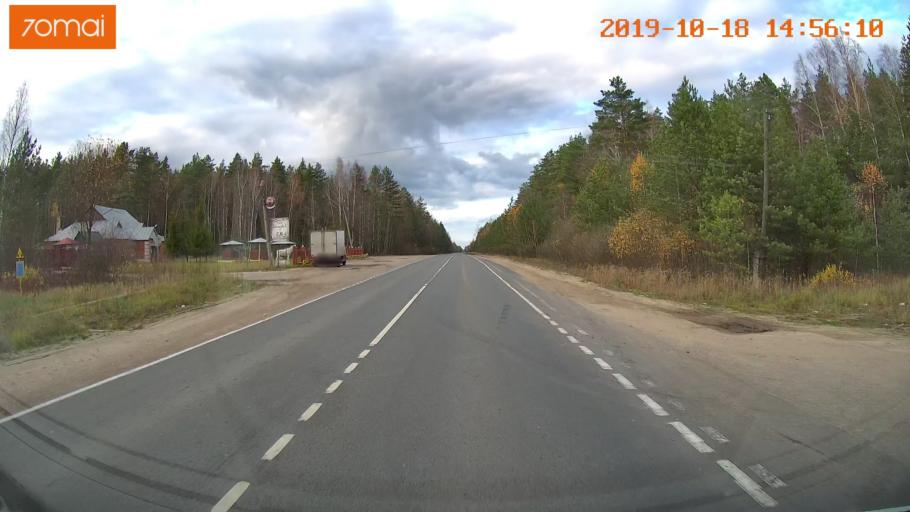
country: RU
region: Vladimir
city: Kurlovo
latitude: 55.4610
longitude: 40.5888
